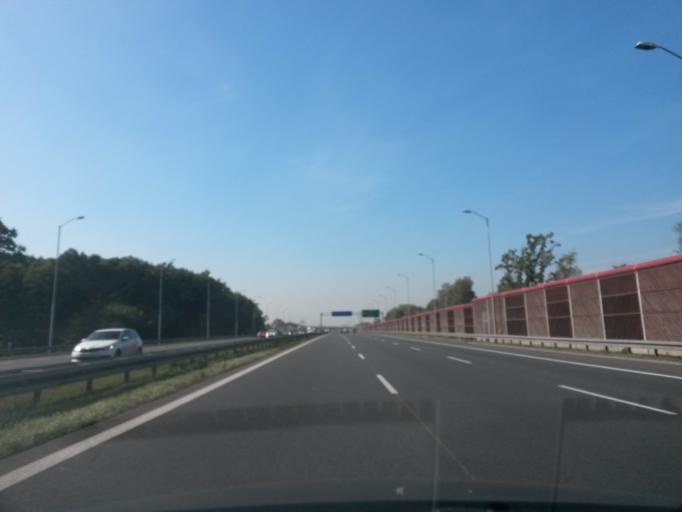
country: PL
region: Silesian Voivodeship
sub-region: Ruda Slaska
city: Ruda Slaska
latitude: 50.2545
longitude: 18.8654
